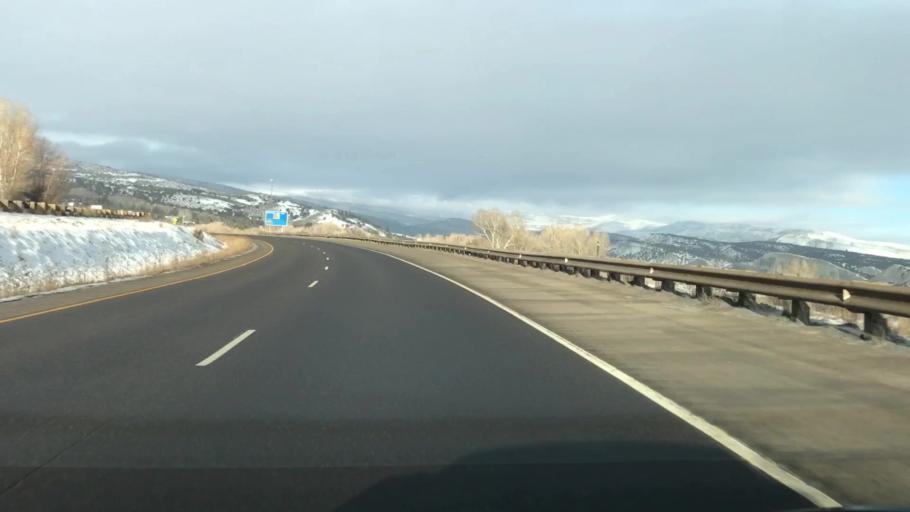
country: US
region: Colorado
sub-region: Eagle County
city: Edwards
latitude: 39.6820
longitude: -106.6506
